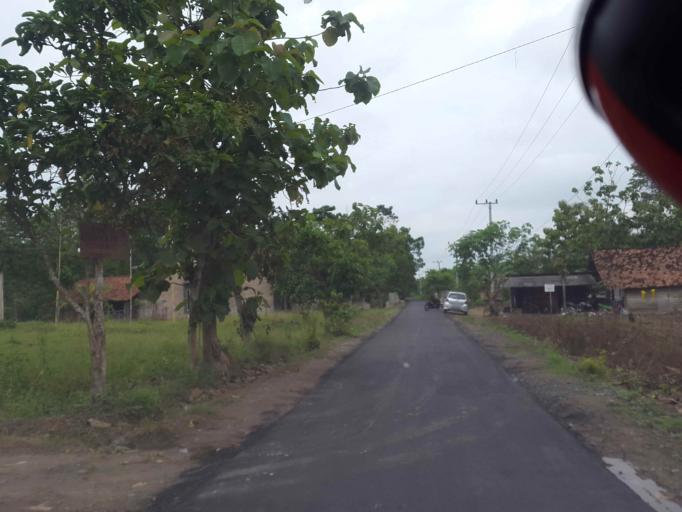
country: ID
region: Lampung
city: Natar
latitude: -5.2649
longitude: 105.2044
